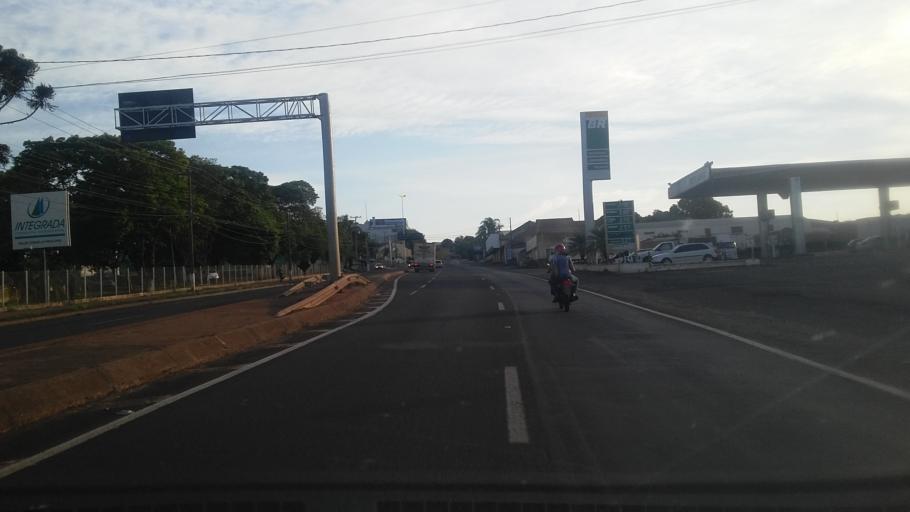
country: BR
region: Parana
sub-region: Assai
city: Assai
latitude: -23.1952
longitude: -50.6527
